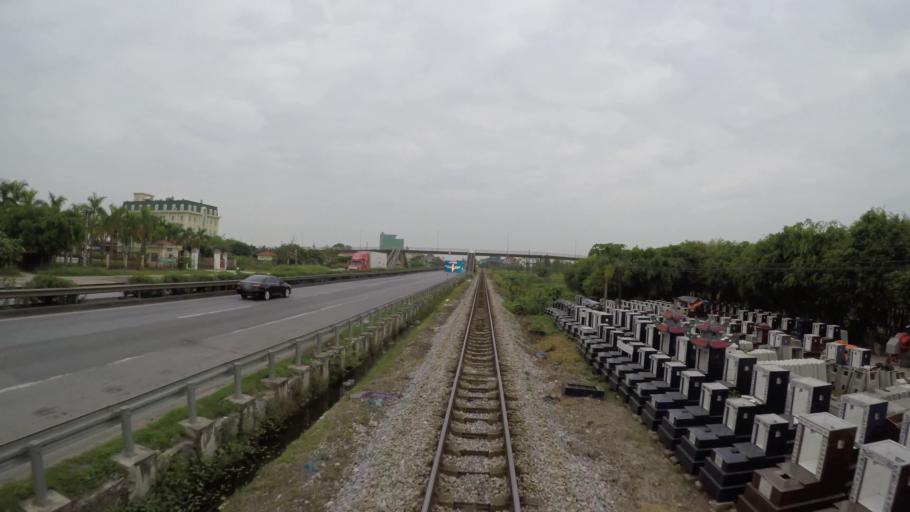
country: VN
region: Hai Duong
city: Phu Thai
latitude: 20.9562
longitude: 106.5269
